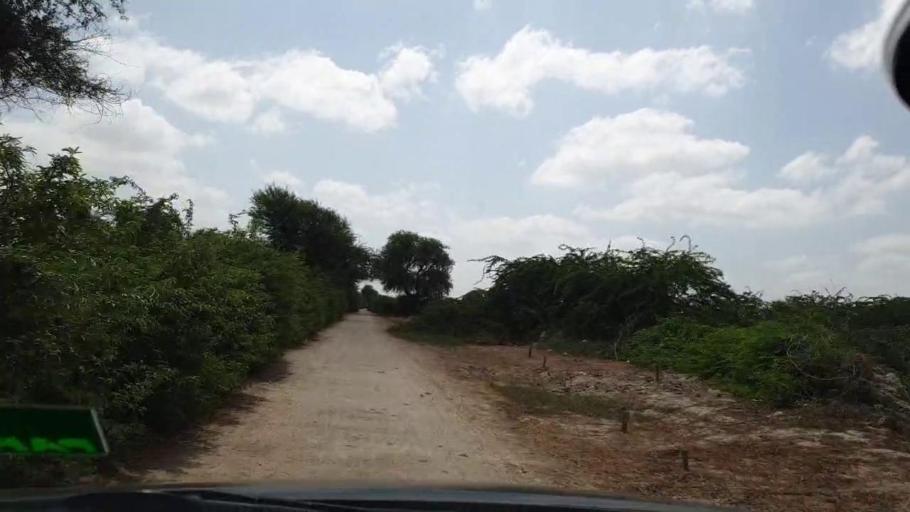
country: PK
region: Sindh
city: Kadhan
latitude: 24.5619
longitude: 69.2112
